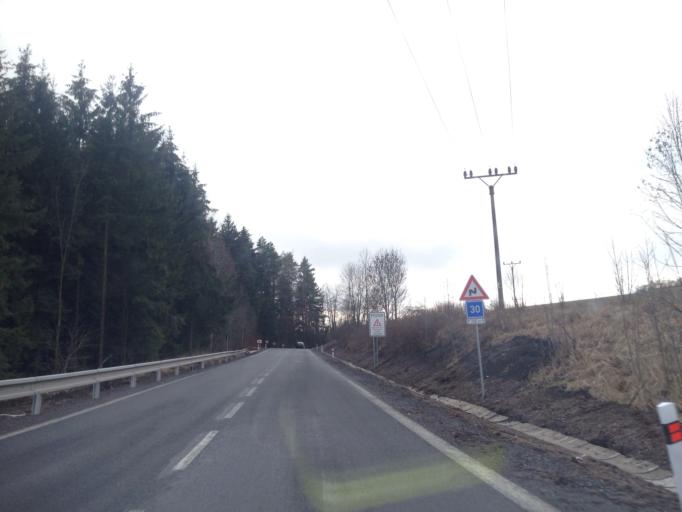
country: CZ
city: Horni Branna
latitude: 50.5827
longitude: 15.5742
